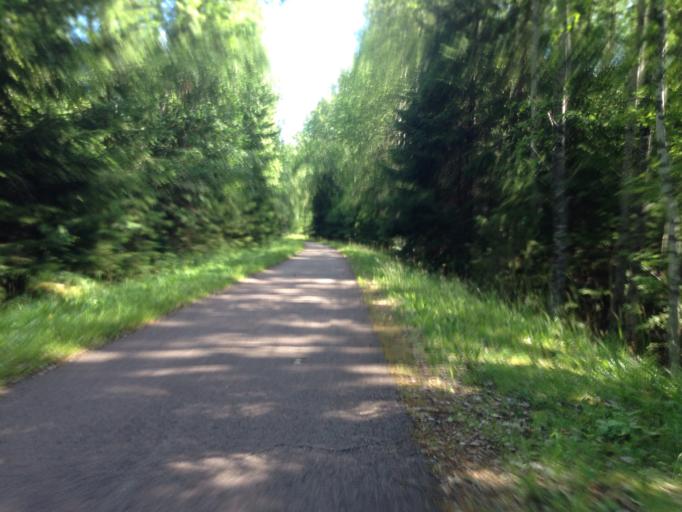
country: SE
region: Dalarna
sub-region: Ludvika Kommun
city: Grangesberg
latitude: 60.2106
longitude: 15.0496
